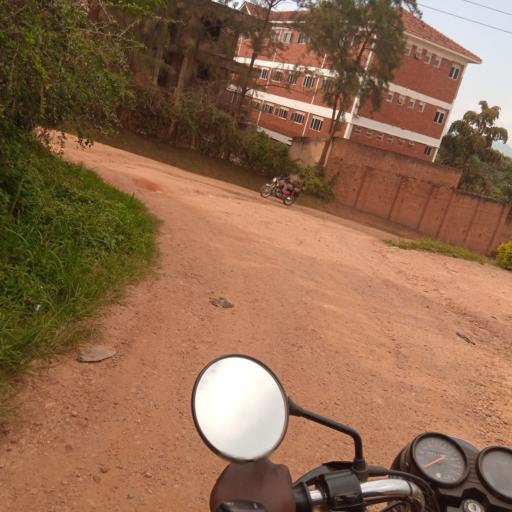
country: UG
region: Eastern Region
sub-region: Mbale District
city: Mbale
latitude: 1.0729
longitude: 34.1841
